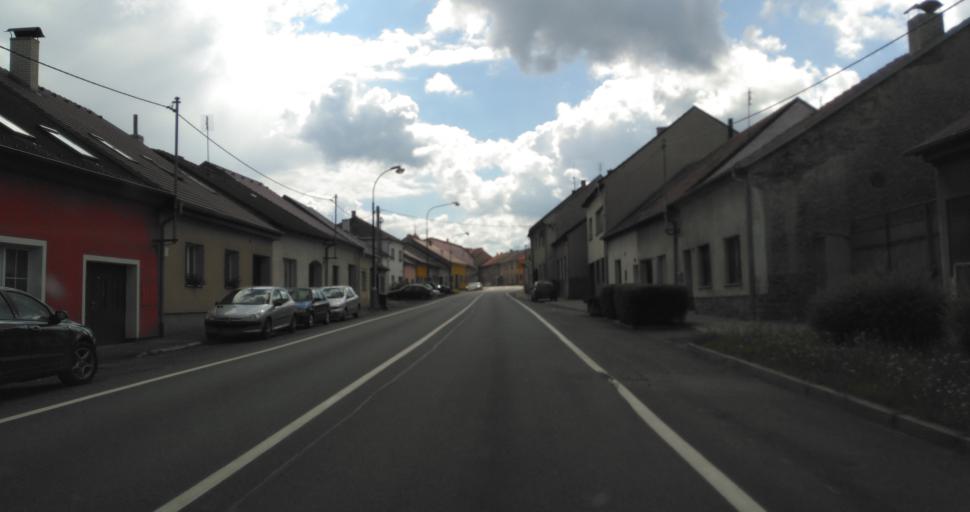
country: CZ
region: Central Bohemia
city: Komarov
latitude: 49.8519
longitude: 13.8388
